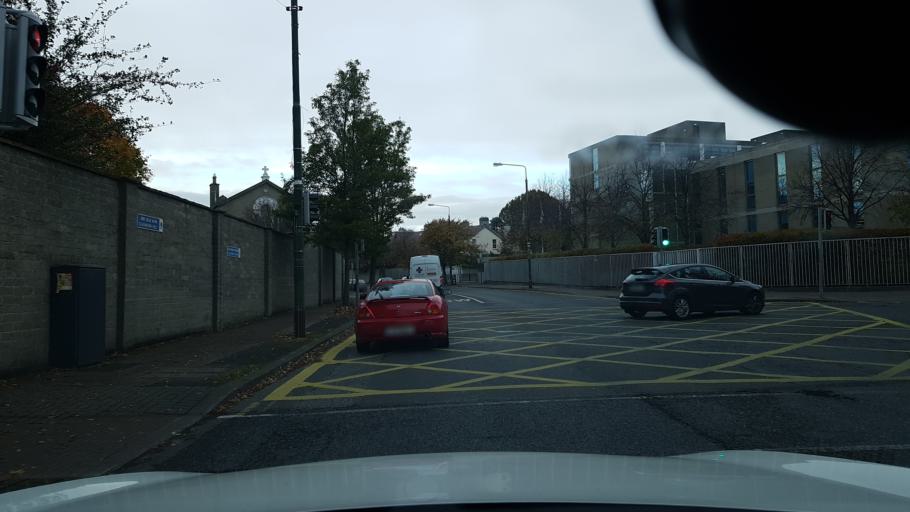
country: IE
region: Leinster
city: Glasnevin
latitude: 53.3757
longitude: -6.2701
